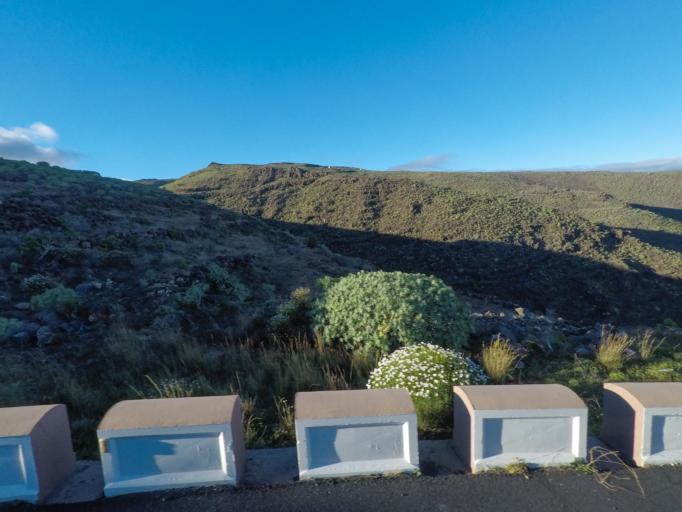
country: ES
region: Canary Islands
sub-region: Provincia de Santa Cruz de Tenerife
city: San Sebastian de la Gomera
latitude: 28.0866
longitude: -17.1427
